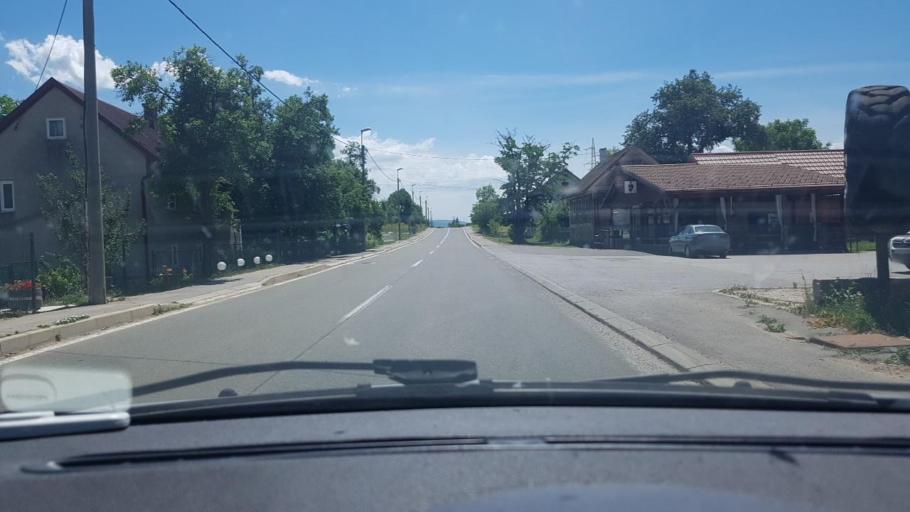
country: HR
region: Licko-Senjska
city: Otocac
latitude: 44.8650
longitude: 15.2583
